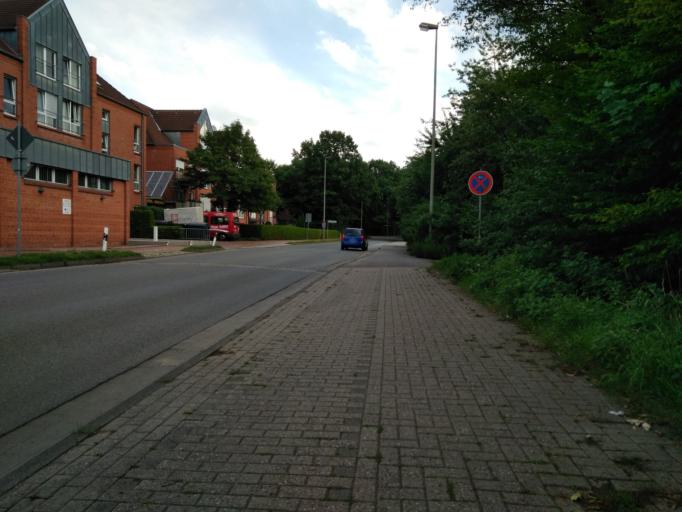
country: DE
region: North Rhine-Westphalia
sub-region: Regierungsbezirk Dusseldorf
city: Schermbeck
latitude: 51.6900
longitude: 6.8660
